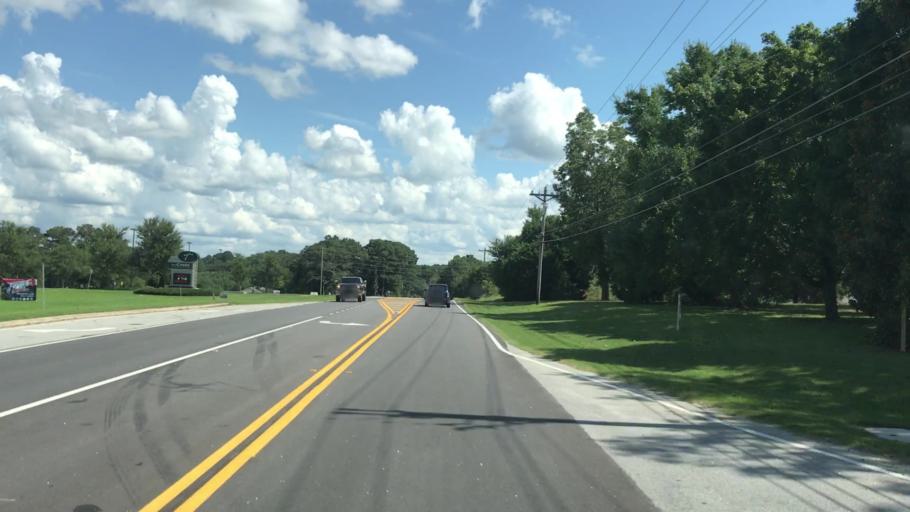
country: US
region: Georgia
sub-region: Walton County
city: Loganville
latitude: 33.8156
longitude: -83.8756
